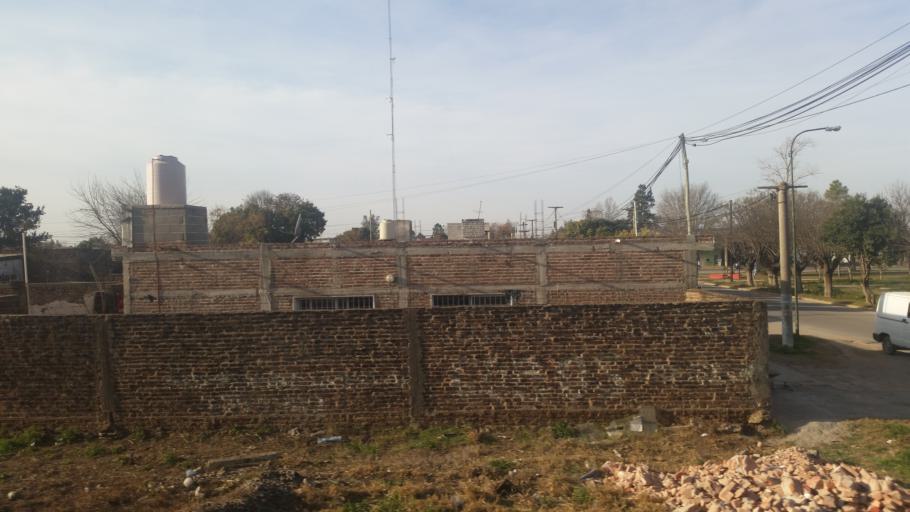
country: AR
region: Cordoba
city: Toledo
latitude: -31.5541
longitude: -64.0116
